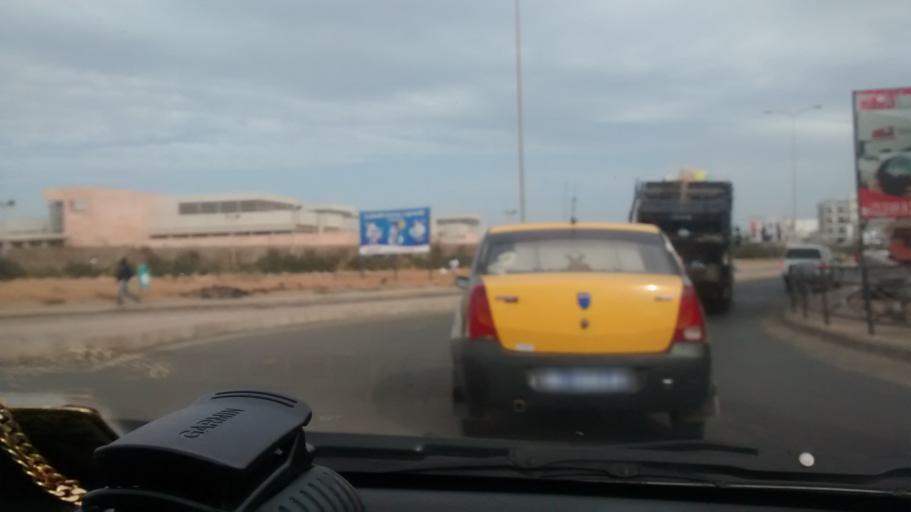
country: SN
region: Dakar
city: Pikine
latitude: 14.7708
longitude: -17.4082
